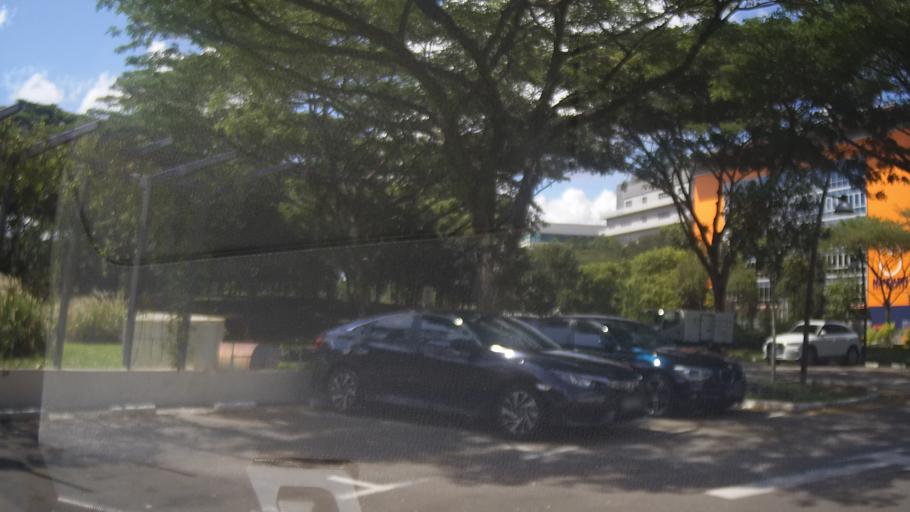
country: MY
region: Johor
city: Johor Bahru
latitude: 1.4439
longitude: 103.7818
